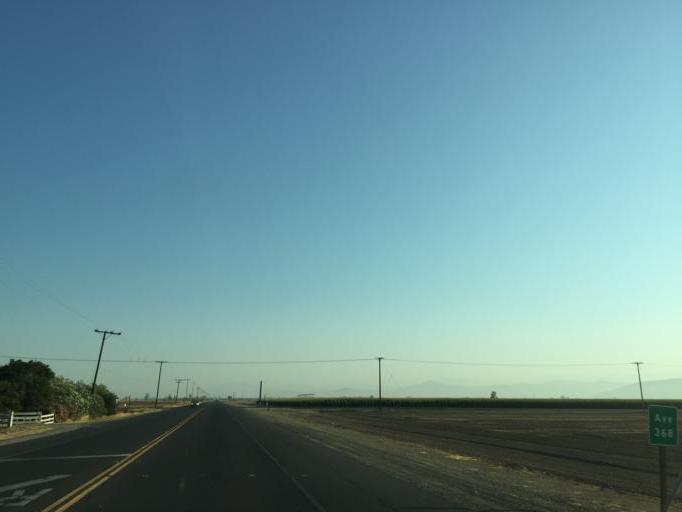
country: US
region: California
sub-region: Tulare County
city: Cutler
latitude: 36.4564
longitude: -119.2954
